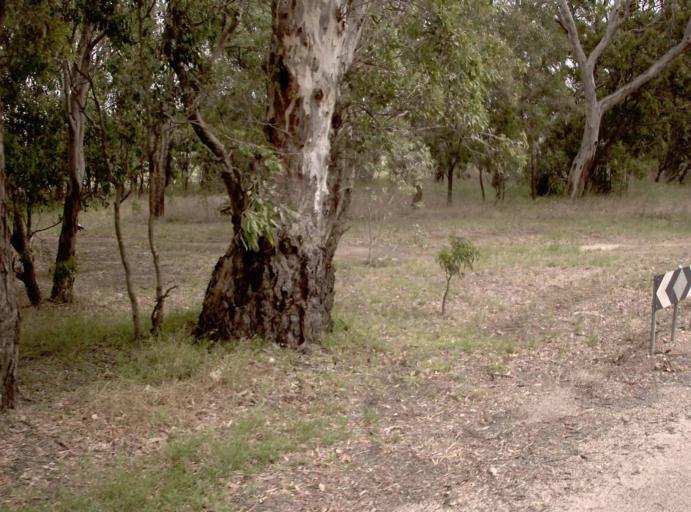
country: AU
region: Victoria
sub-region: Wellington
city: Sale
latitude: -37.9359
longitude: 147.0956
